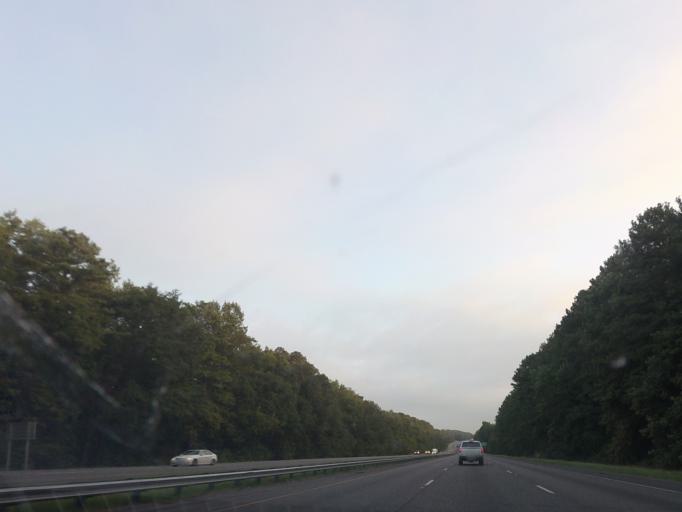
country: US
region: Georgia
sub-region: Monroe County
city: Forsyth
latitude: 33.0993
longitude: -83.9995
